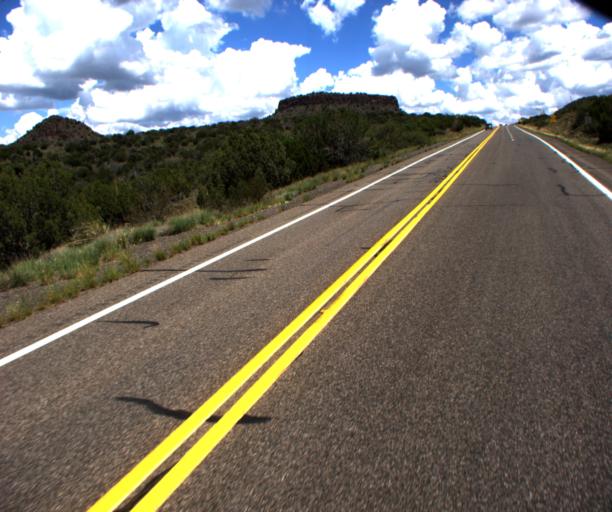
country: US
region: Arizona
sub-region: Yavapai County
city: Lake Montezuma
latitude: 34.4924
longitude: -111.6887
